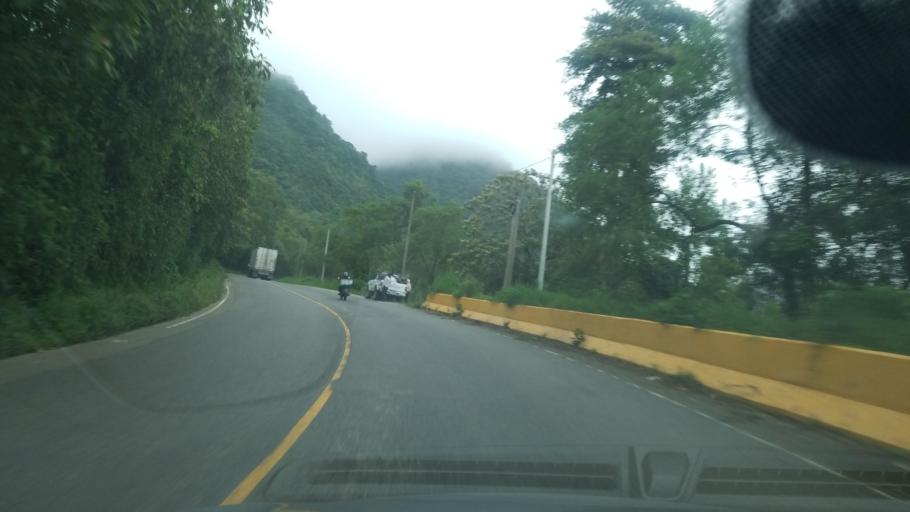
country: HN
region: Ocotepeque
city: La Labor
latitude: 14.4765
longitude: -89.0579
